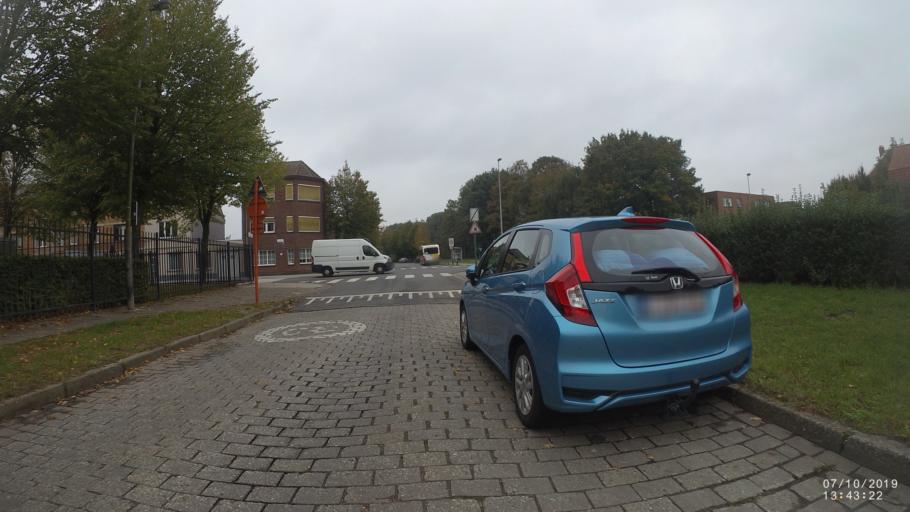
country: BE
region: Flanders
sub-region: Provincie Oost-Vlaanderen
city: Gent
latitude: 51.0761
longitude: 3.7156
